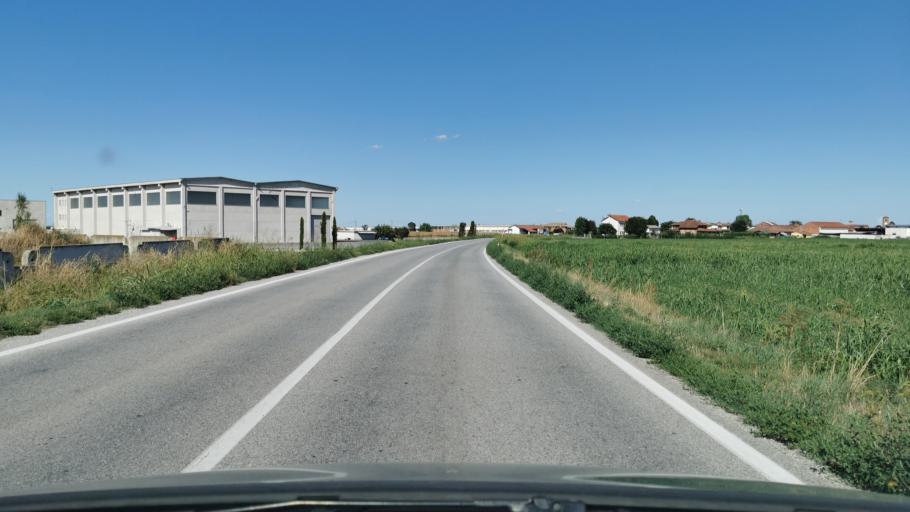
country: IT
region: Piedmont
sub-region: Provincia di Cuneo
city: Genola
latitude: 44.5857
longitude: 7.6485
